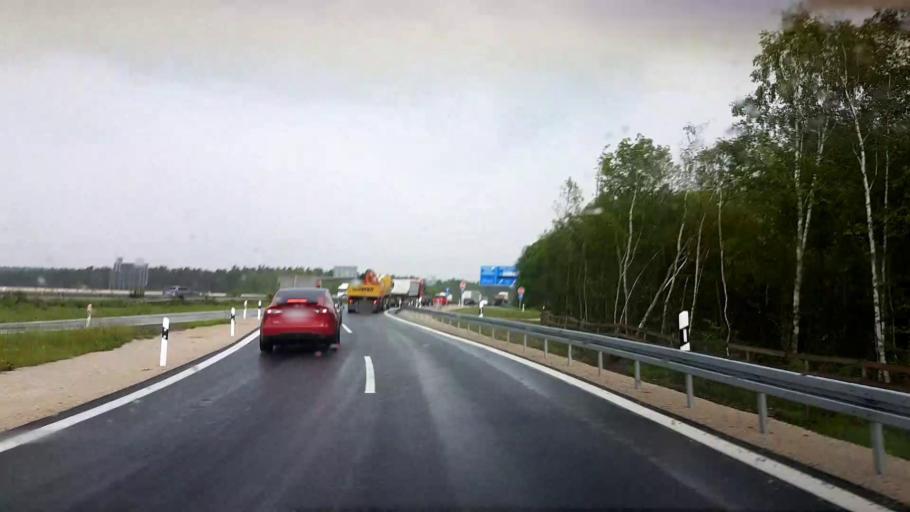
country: DE
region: Bavaria
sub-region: Regierungsbezirk Mittelfranken
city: Feucht
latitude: 49.3947
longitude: 11.1973
